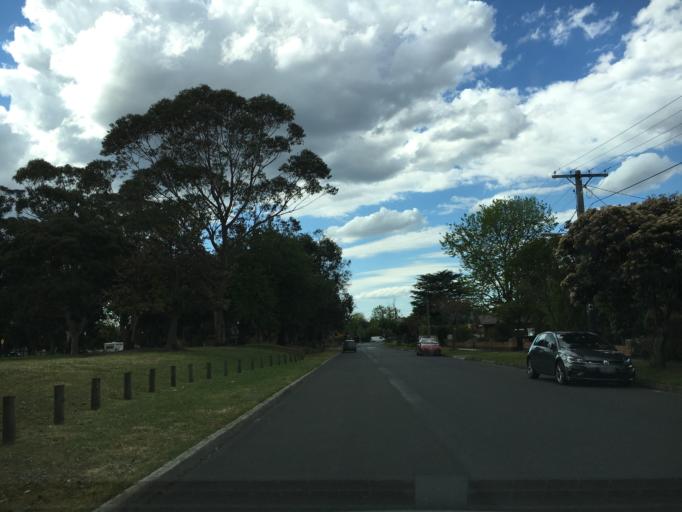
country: AU
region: Victoria
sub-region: Monash
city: Oakleigh South
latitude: -37.9122
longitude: 145.0939
